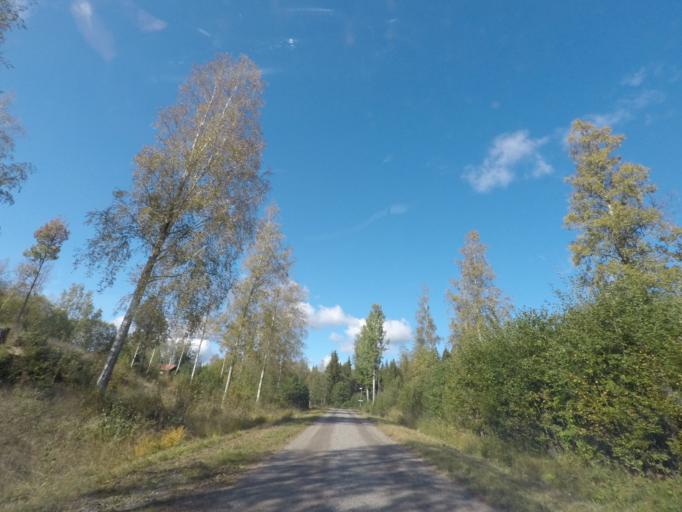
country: SE
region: Vaestmanland
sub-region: Skinnskattebergs Kommun
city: Skinnskatteberg
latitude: 59.8302
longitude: 15.5209
